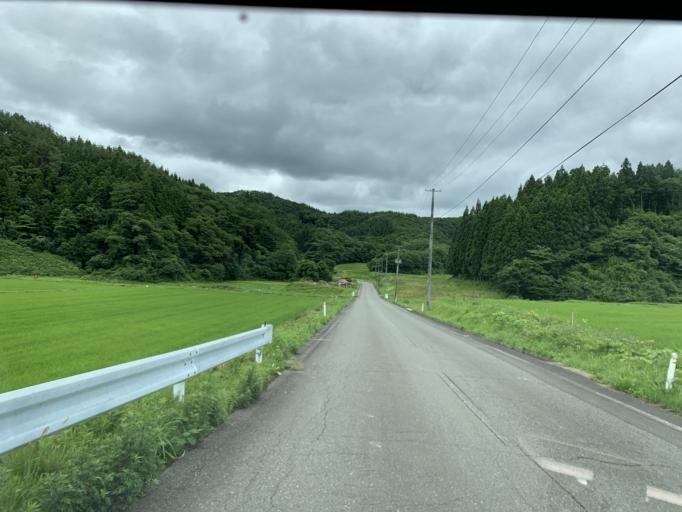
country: JP
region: Iwate
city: Ichinoseki
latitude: 38.9010
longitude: 140.9793
